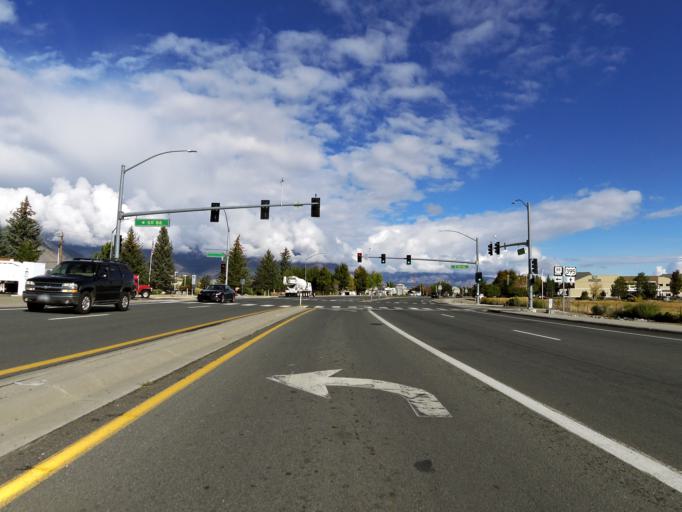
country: US
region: Nevada
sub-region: Douglas County
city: Minden
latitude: 38.9605
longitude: -119.7784
